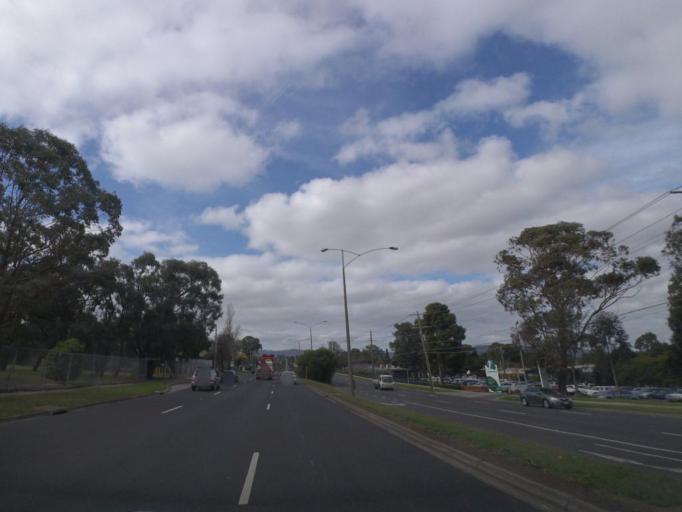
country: AU
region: Victoria
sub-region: Knox
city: Wantirna
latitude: -37.8323
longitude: 145.2226
